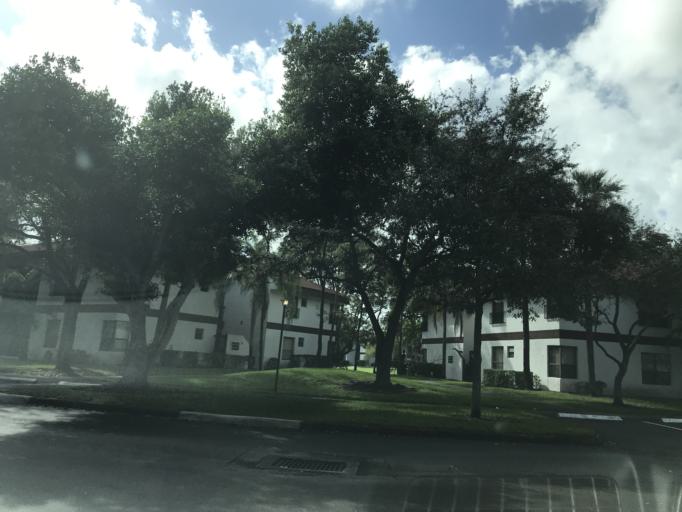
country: US
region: Florida
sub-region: Broward County
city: Coconut Creek
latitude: 26.2716
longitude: -80.1868
